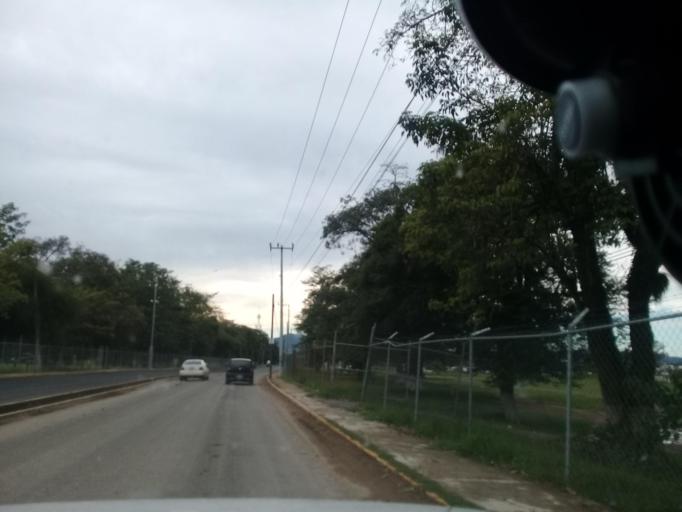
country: MX
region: Hidalgo
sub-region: Huejutla de Reyes
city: Parque de Poblamiento Solidaridad
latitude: 21.1545
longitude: -98.3831
